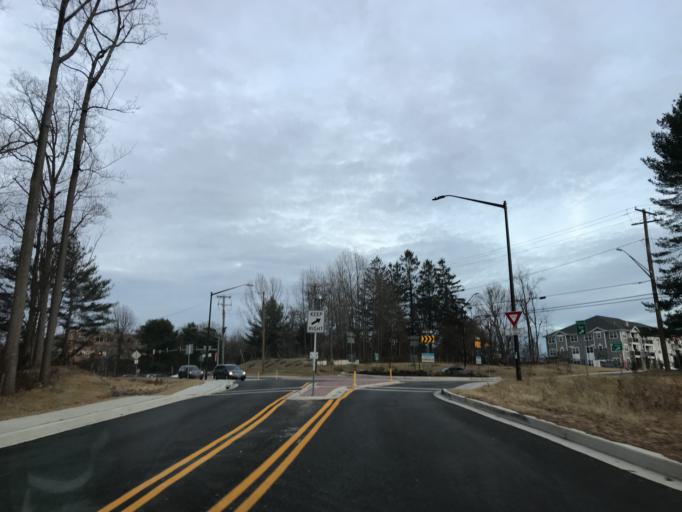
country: US
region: Maryland
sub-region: Harford County
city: Bel Air South
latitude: 39.5009
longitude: -76.3340
